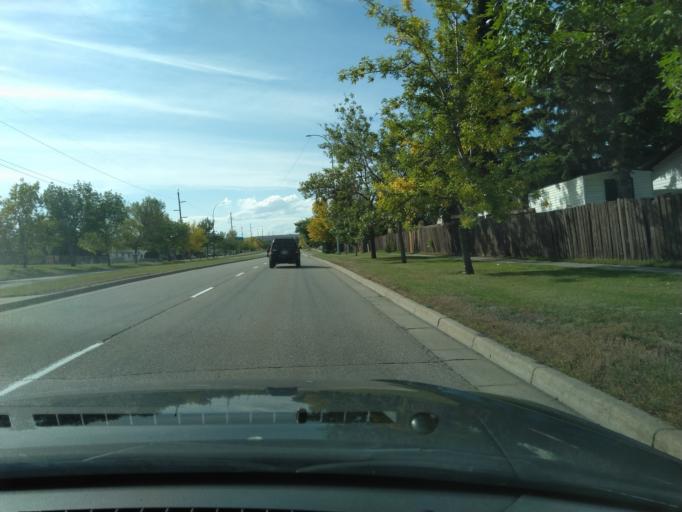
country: CA
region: Alberta
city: Calgary
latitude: 51.1252
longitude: -114.0641
